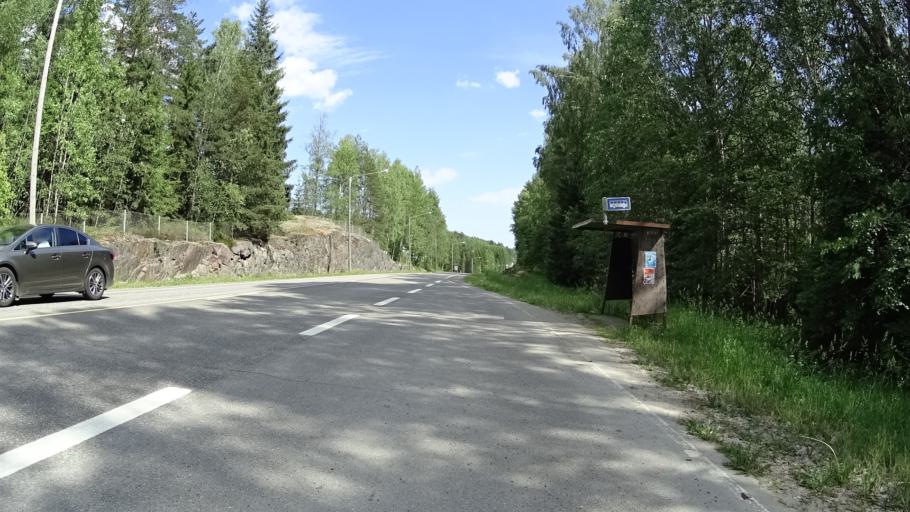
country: FI
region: Uusimaa
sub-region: Raaseporin
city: Karis
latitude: 60.0975
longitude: 23.5973
